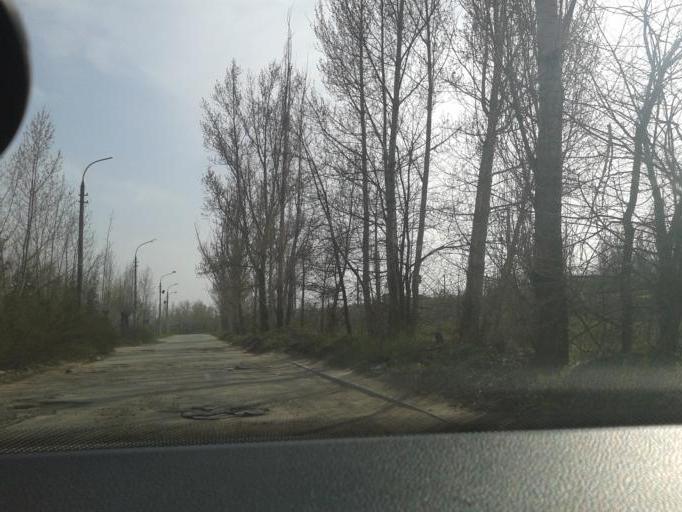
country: RU
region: Volgograd
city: Volgograd
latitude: 48.6333
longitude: 44.4378
